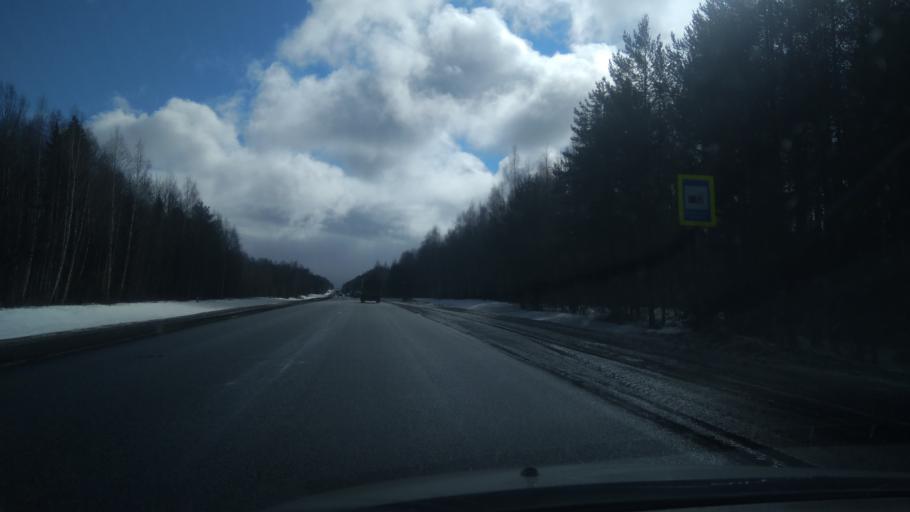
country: RU
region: Perm
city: Kungur
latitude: 57.4236
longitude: 56.8408
